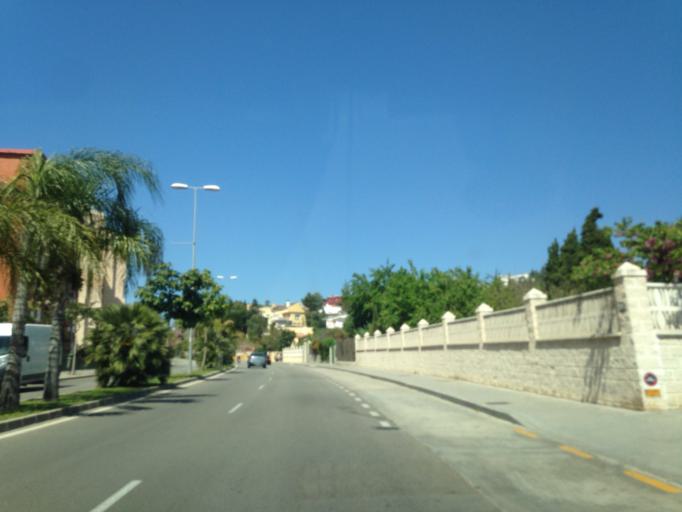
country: ES
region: Andalusia
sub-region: Provincia de Malaga
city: Malaga
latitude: 36.7317
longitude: -4.4700
